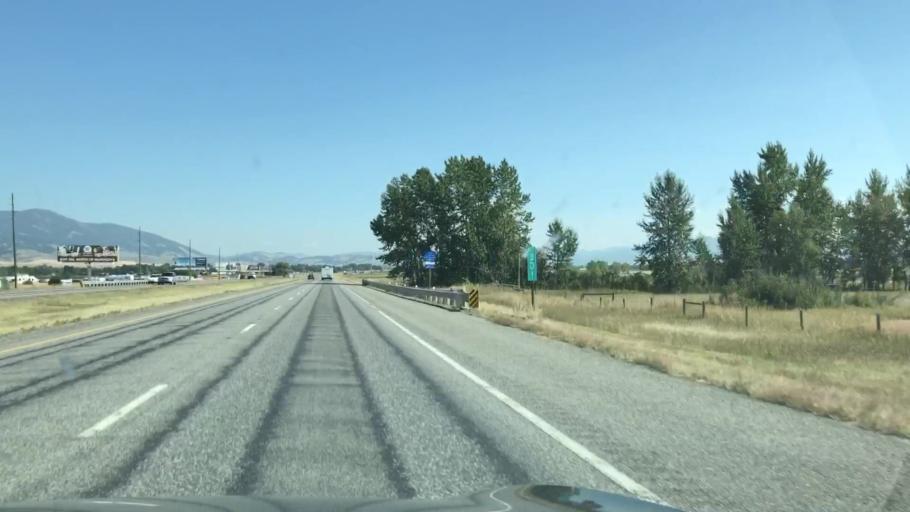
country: US
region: Montana
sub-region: Gallatin County
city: Belgrade
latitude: 45.7506
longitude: -111.1351
